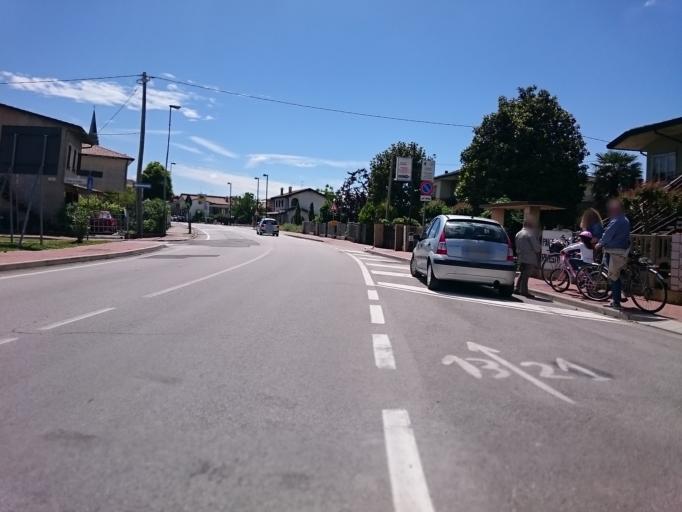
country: IT
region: Veneto
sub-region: Provincia di Padova
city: Campagnola
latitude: 45.2807
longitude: 11.9952
